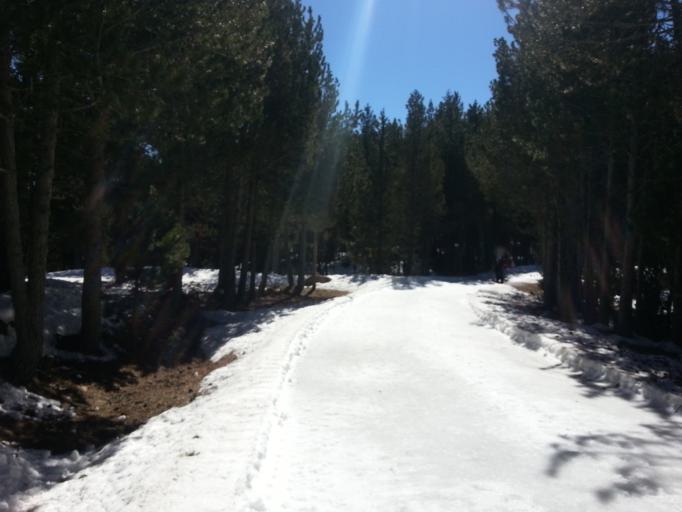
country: ES
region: Catalonia
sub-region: Provincia de Girona
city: Llivia
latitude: 42.5874
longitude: 2.0528
